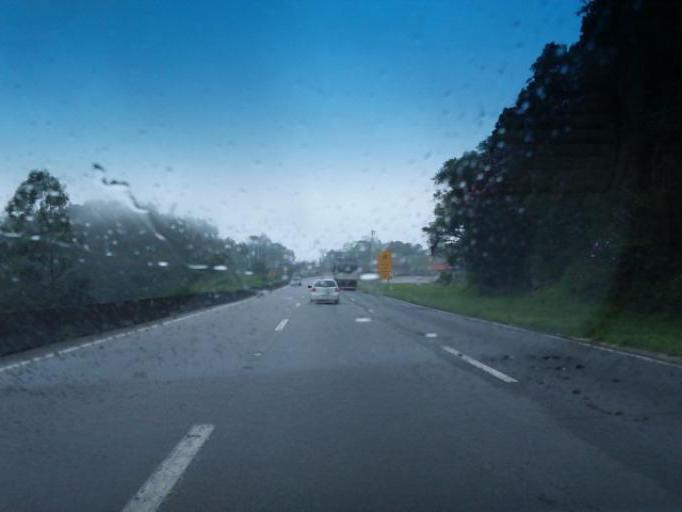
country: BR
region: Parana
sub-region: Campina Grande Do Sul
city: Campina Grande do Sul
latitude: -25.1079
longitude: -48.8198
